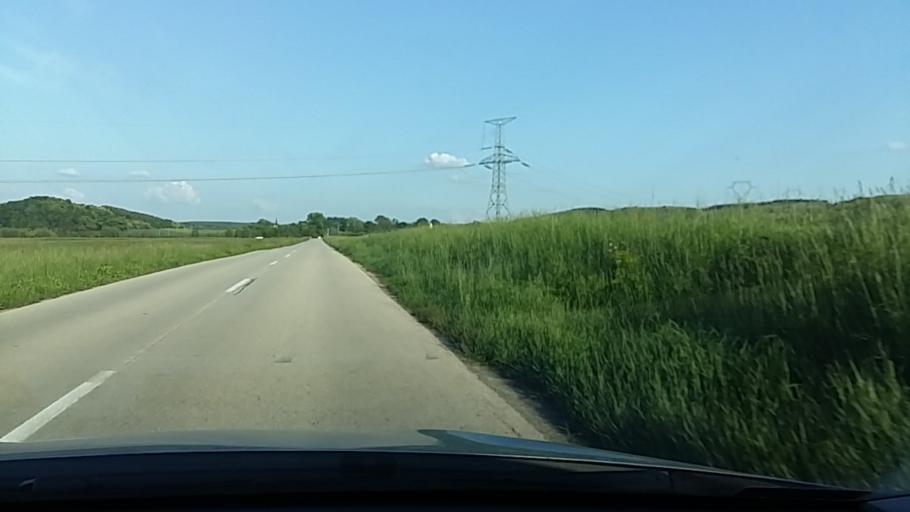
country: HU
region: Pest
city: Szod
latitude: 47.7541
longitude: 19.1988
